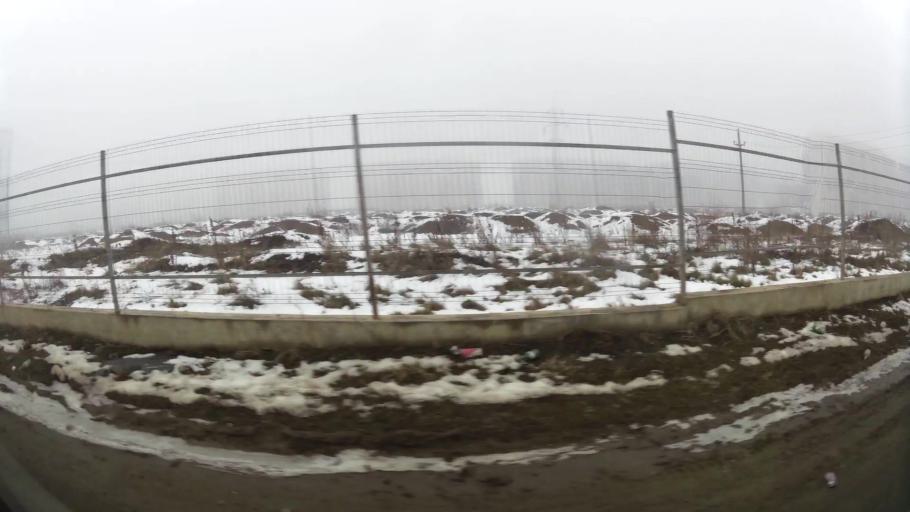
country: RO
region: Ilfov
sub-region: Comuna Chiajna
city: Chiajna
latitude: 44.4414
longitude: 25.9787
